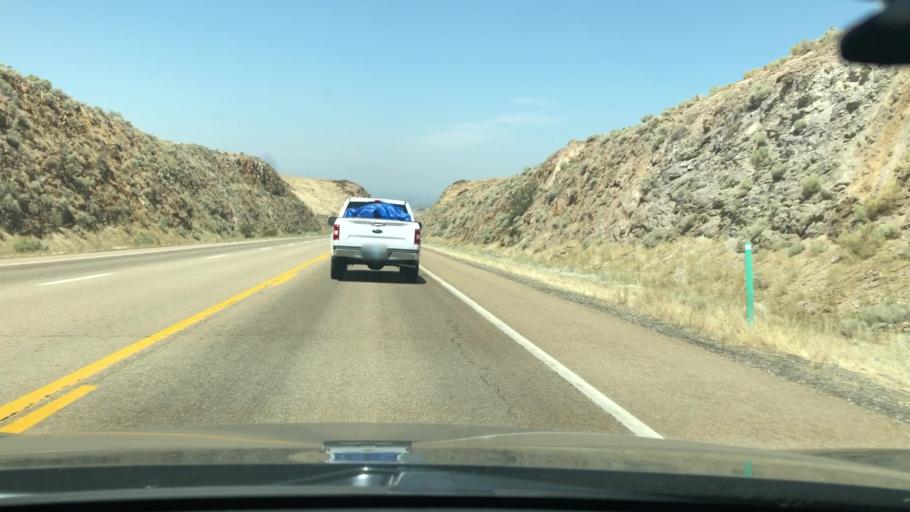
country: US
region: Idaho
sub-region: Owyhee County
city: Marsing
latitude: 43.4286
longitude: -116.8592
